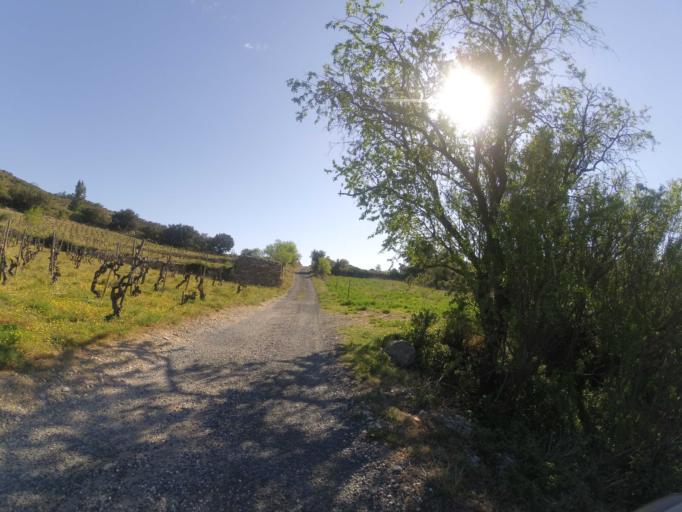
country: FR
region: Languedoc-Roussillon
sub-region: Departement des Pyrenees-Orientales
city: Baixas
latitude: 42.7620
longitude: 2.7610
